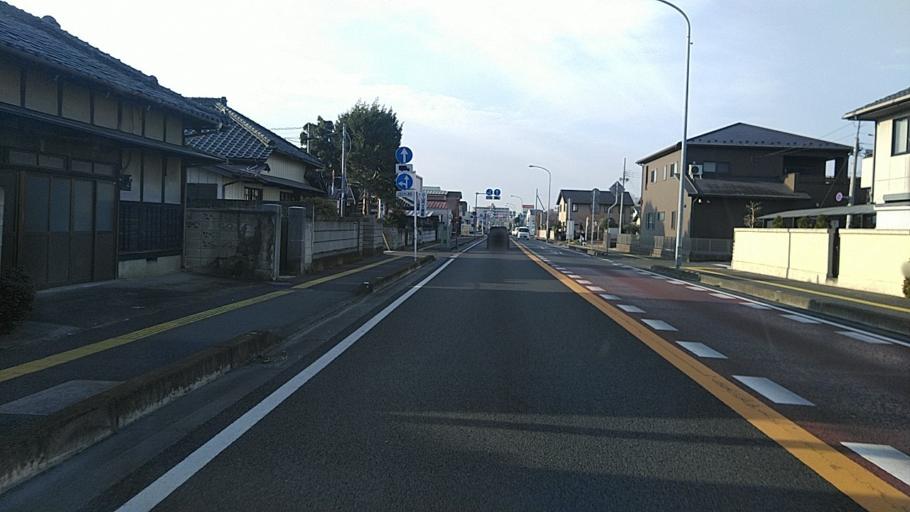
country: JP
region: Tochigi
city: Oyama
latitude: 36.3101
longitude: 139.7984
